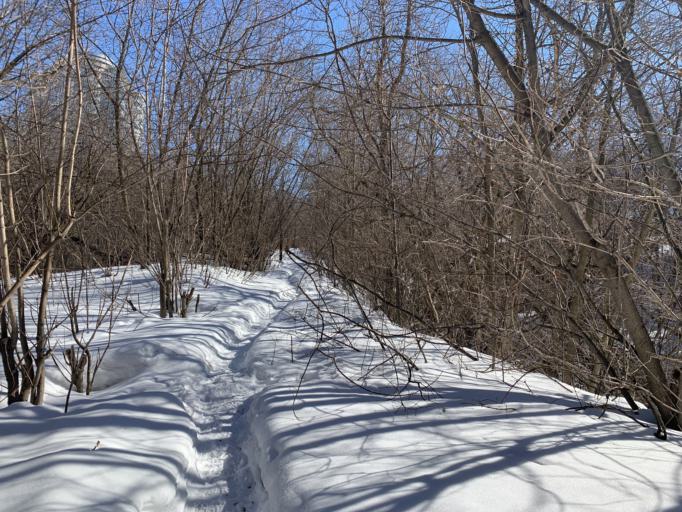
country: RU
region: Chuvashia
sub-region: Cheboksarskiy Rayon
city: Cheboksary
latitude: 56.1452
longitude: 47.2619
